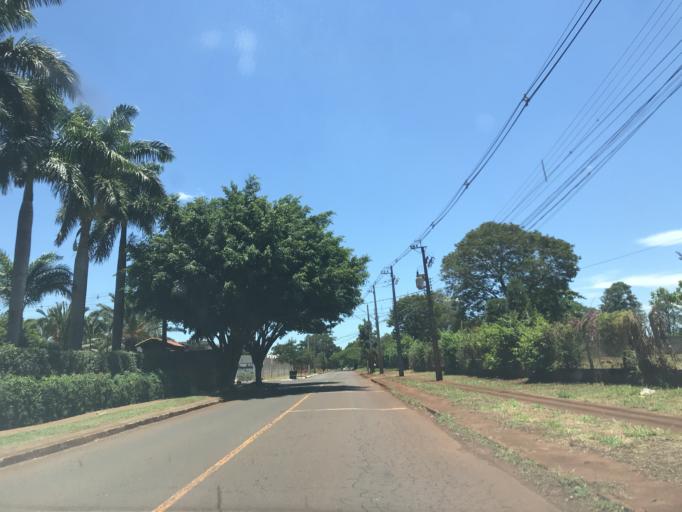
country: BR
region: Parana
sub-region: Sarandi
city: Sarandi
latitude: -23.4442
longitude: -51.9069
